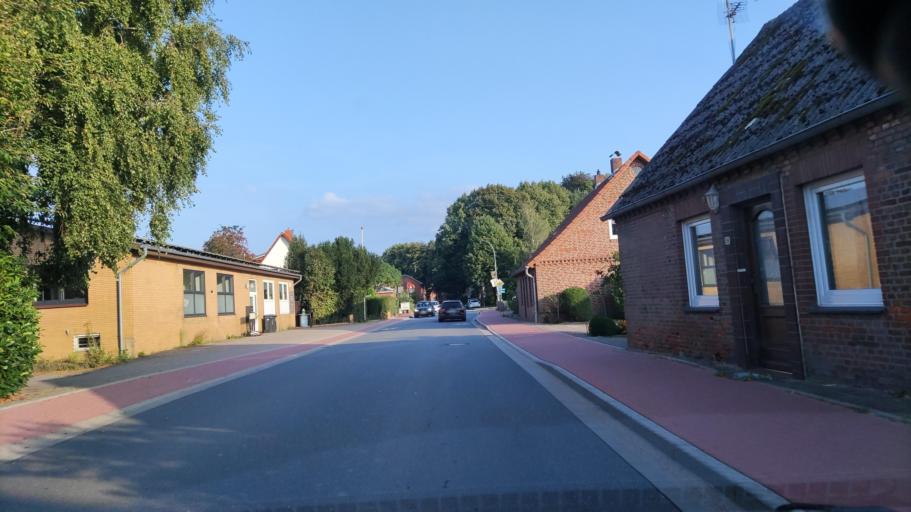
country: DE
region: Schleswig-Holstein
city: Itzstedt
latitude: 53.8256
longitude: 10.1471
